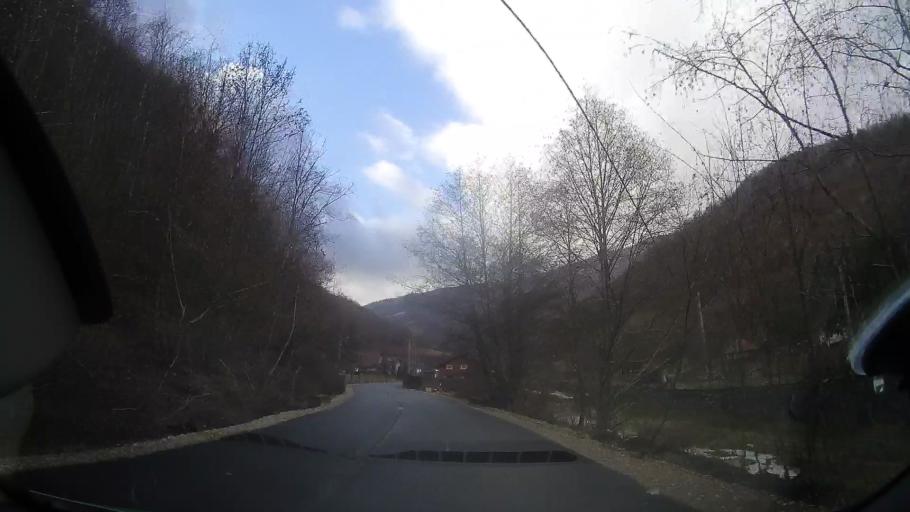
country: RO
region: Cluj
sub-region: Comuna Valea Ierii
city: Valea Ierii
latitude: 46.6856
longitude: 23.2858
